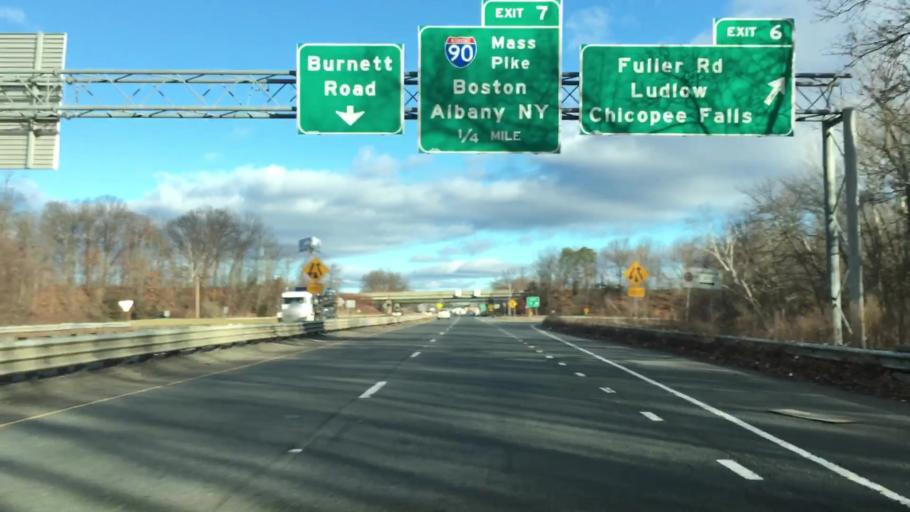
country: US
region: Massachusetts
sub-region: Hampden County
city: North Chicopee
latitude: 42.1596
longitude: -72.5477
